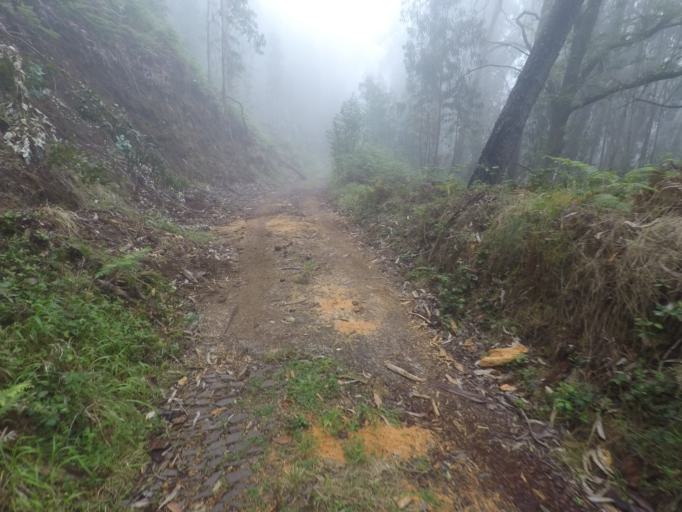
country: PT
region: Madeira
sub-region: Calheta
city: Arco da Calheta
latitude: 32.7258
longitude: -17.0943
